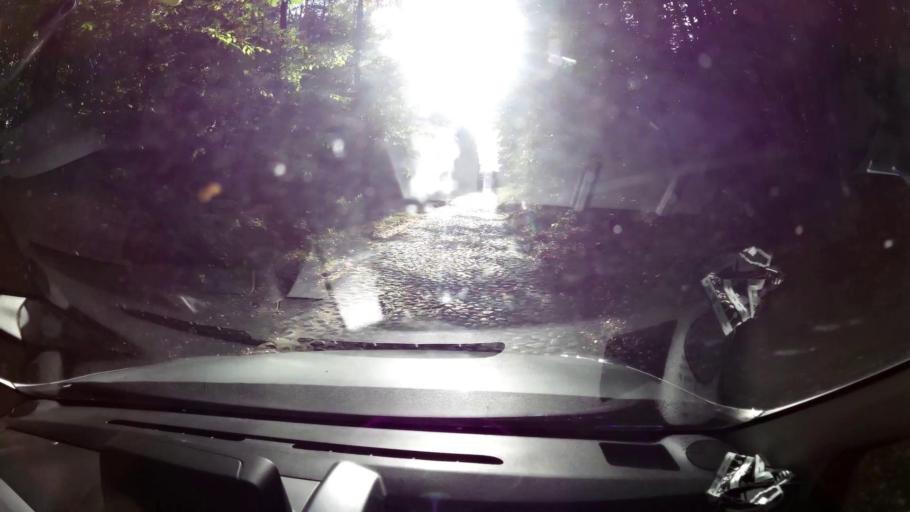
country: PL
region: Pomeranian Voivodeship
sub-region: Powiat bytowski
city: Miastko
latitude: 54.0761
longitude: 16.8831
